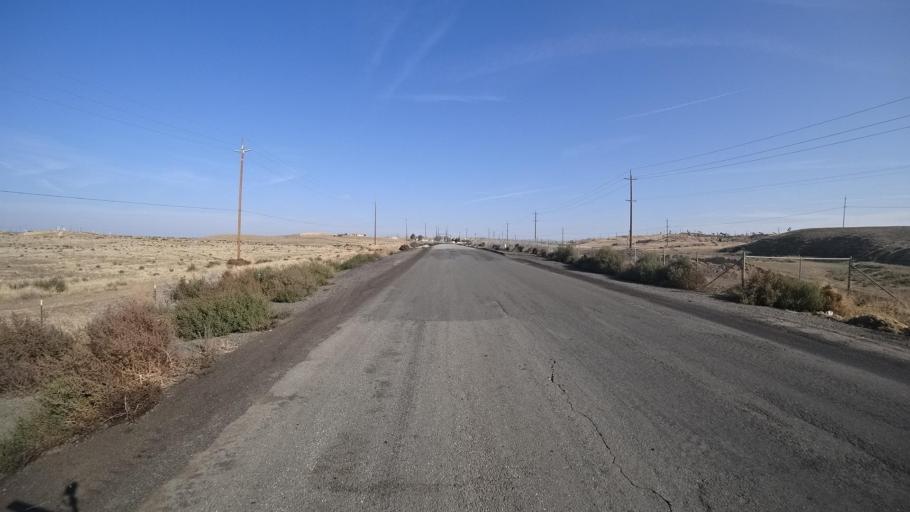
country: US
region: California
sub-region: Kern County
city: Oildale
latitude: 35.4715
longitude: -119.0228
